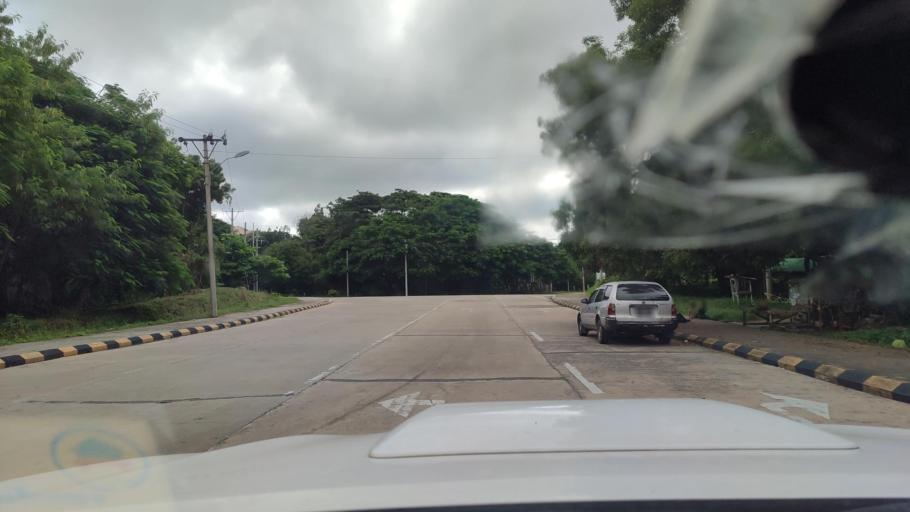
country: MM
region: Mandalay
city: Nay Pyi Taw
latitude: 19.7622
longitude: 96.0792
